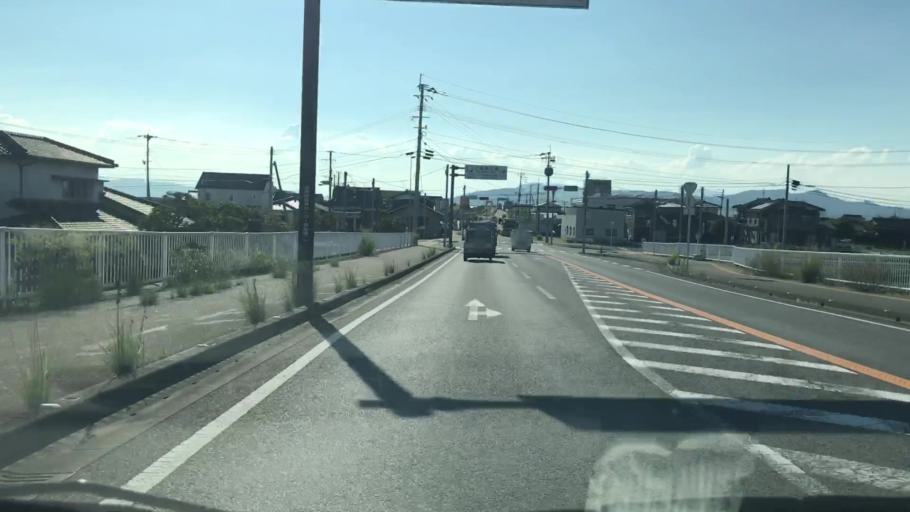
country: JP
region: Saga Prefecture
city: Saga-shi
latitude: 33.2191
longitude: 130.2586
